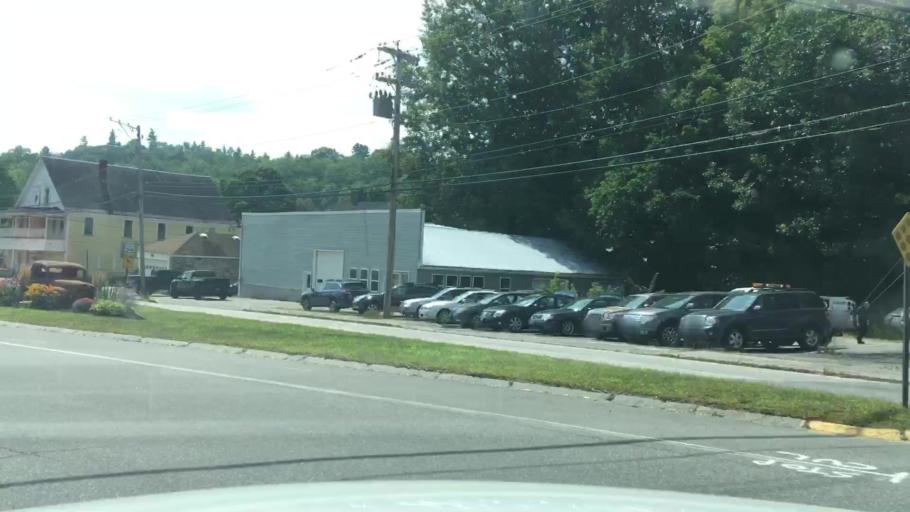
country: US
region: Maine
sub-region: Oxford County
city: Rumford
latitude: 44.5361
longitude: -70.5448
